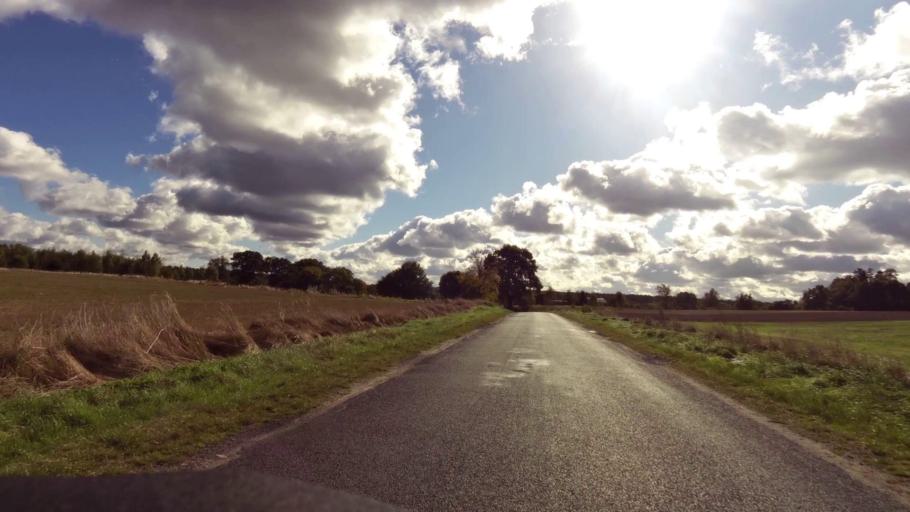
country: PL
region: West Pomeranian Voivodeship
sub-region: Powiat bialogardzki
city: Bialogard
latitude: 53.9940
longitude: 16.0645
